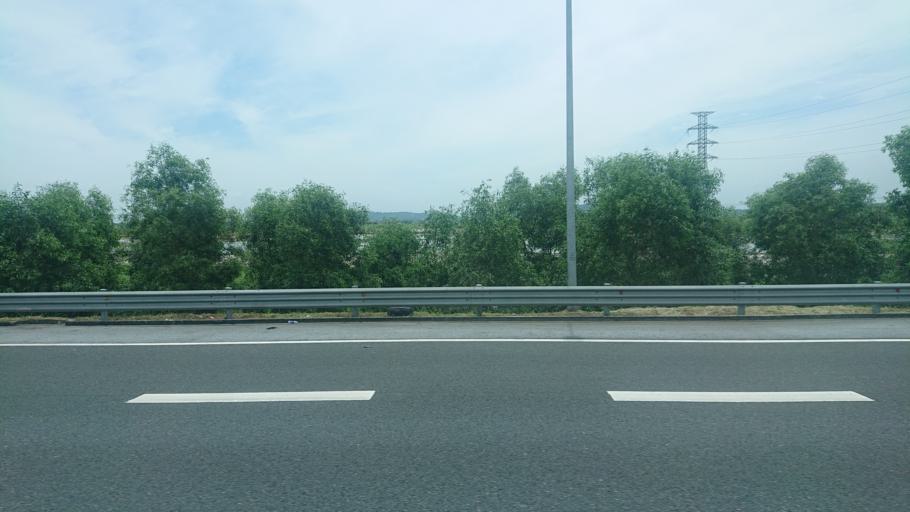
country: VN
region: Hai Phong
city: An Lao
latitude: 20.7917
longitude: 106.5511
